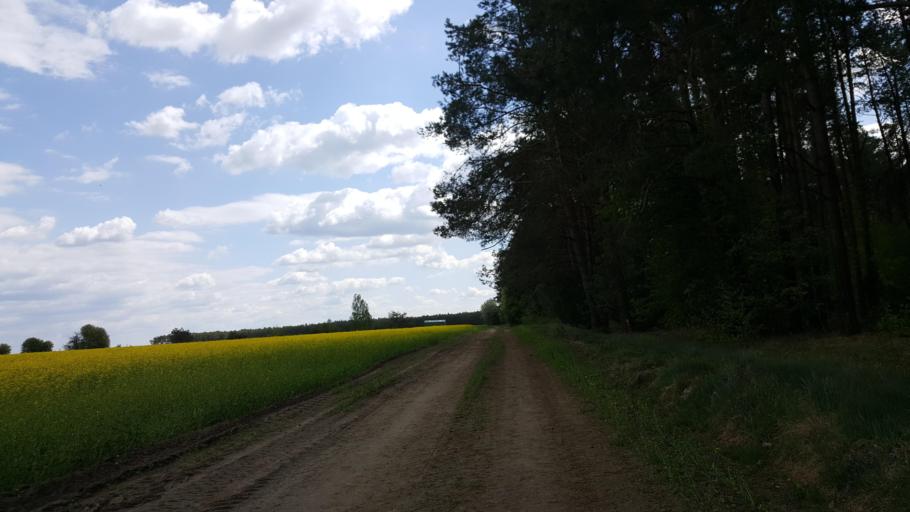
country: BY
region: Brest
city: Kamyanyets
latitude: 52.3872
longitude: 23.9416
